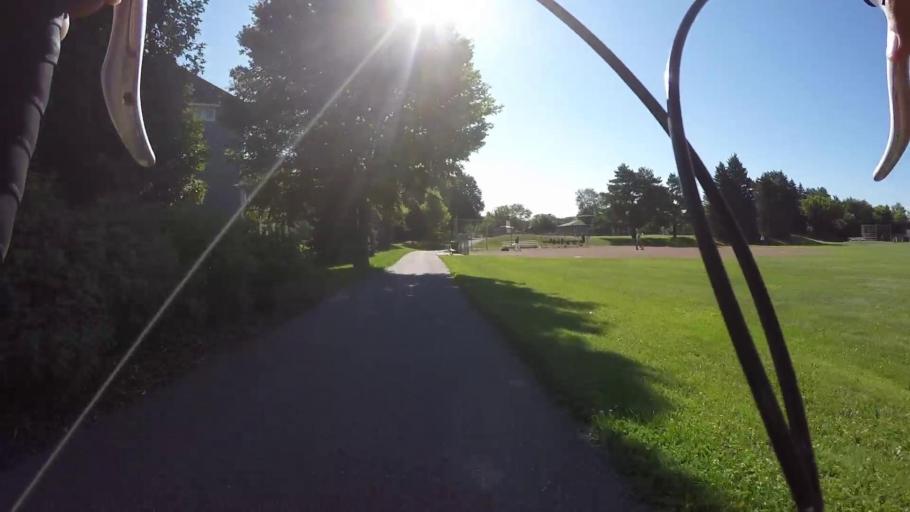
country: US
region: Minnesota
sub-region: Carver County
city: Chanhassen
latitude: 44.8780
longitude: -93.5009
